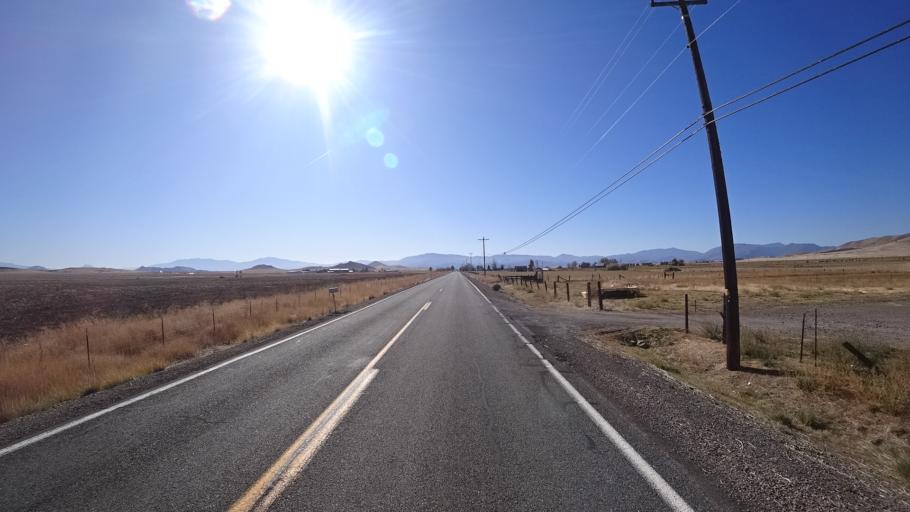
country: US
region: California
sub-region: Siskiyou County
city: Montague
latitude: 41.7763
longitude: -122.4746
